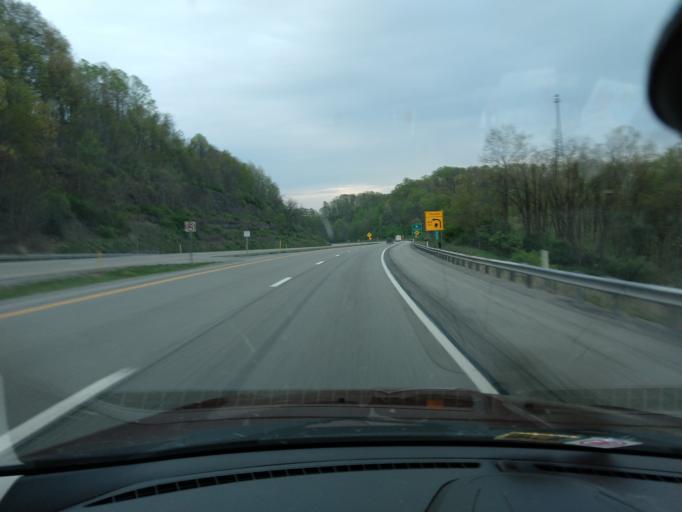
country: US
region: West Virginia
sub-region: Lewis County
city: Weston
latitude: 38.9606
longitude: -80.5243
